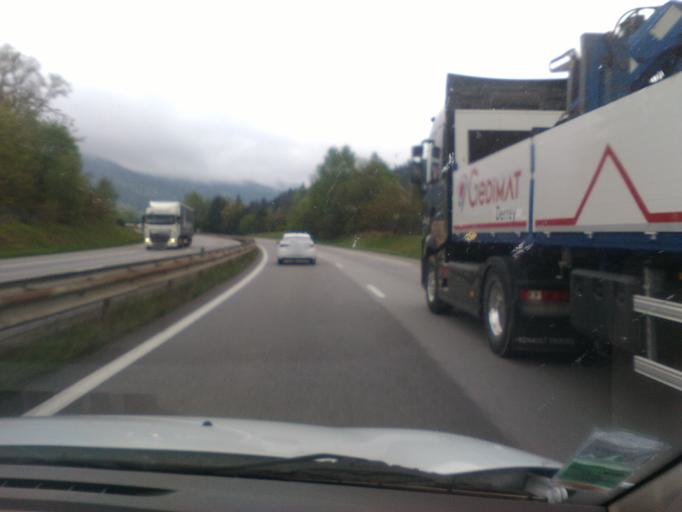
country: FR
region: Lorraine
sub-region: Departement des Vosges
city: Saint-Nabord
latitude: 48.0739
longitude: 6.5935
